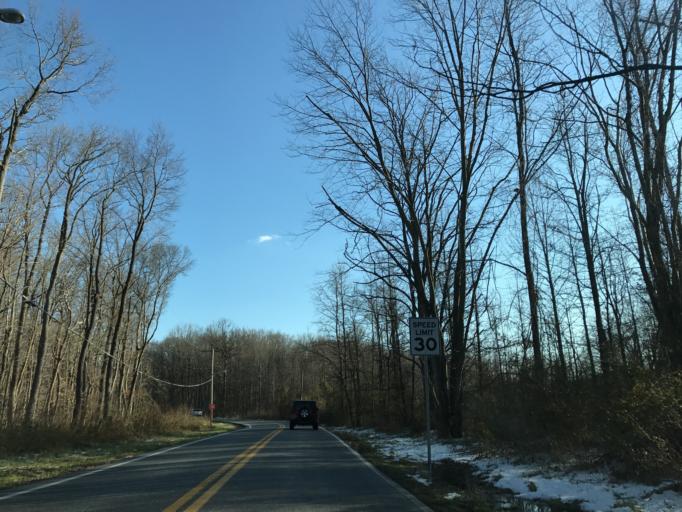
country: US
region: Maryland
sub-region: Baltimore County
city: Essex
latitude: 39.2969
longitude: -76.4412
